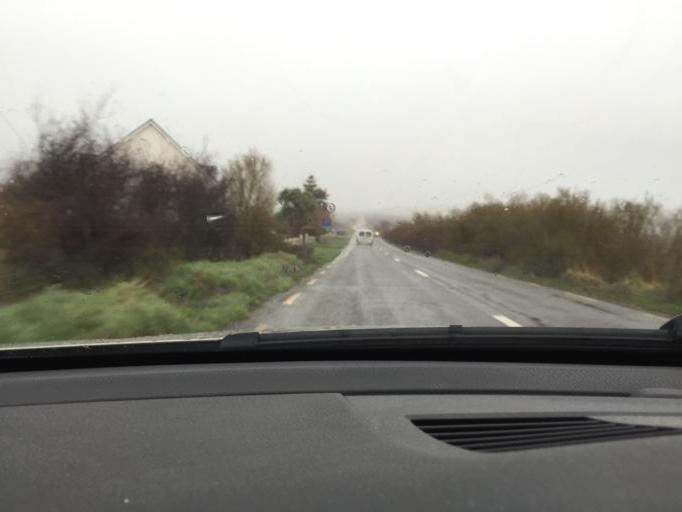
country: IE
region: Munster
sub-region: Ciarrai
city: Dingle
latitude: 52.1405
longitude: -10.2014
